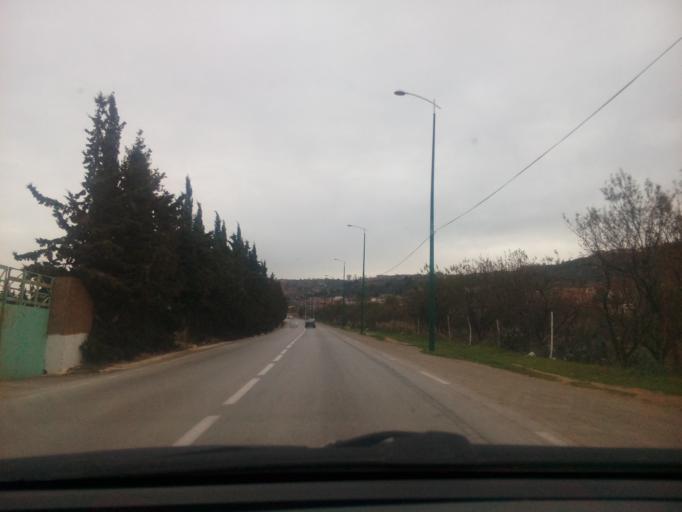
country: DZ
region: Tlemcen
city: Mansoura
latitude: 34.8642
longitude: -1.3446
